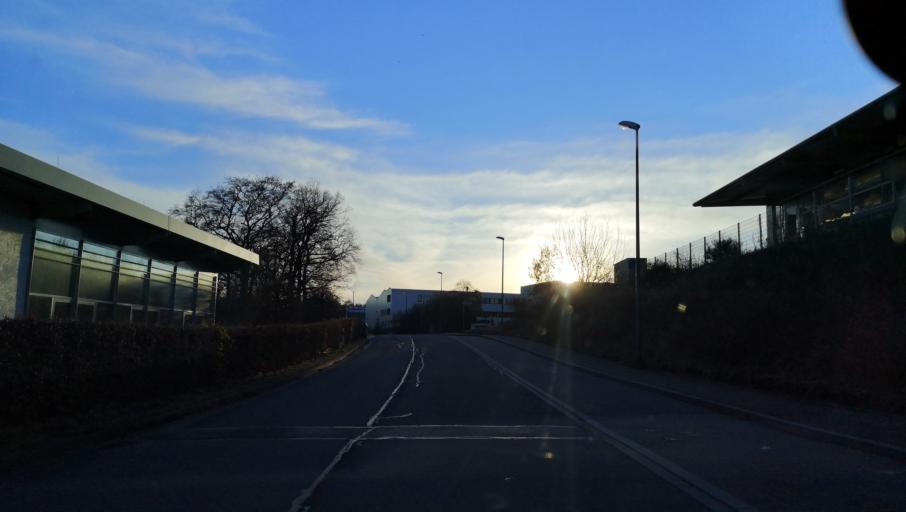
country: DE
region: North Rhine-Westphalia
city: Radevormwald
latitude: 51.1974
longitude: 7.3851
